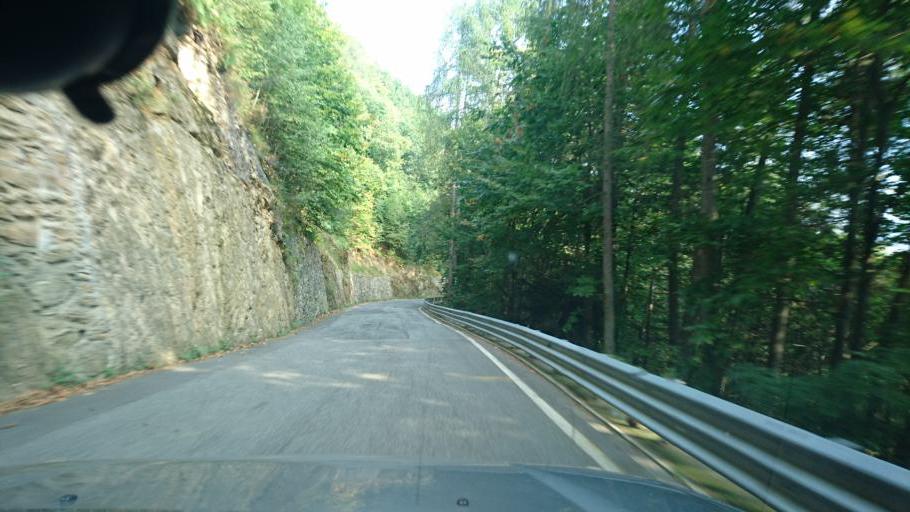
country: IT
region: Lombardy
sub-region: Provincia di Brescia
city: Paisco Loveno
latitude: 46.0853
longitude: 10.3044
